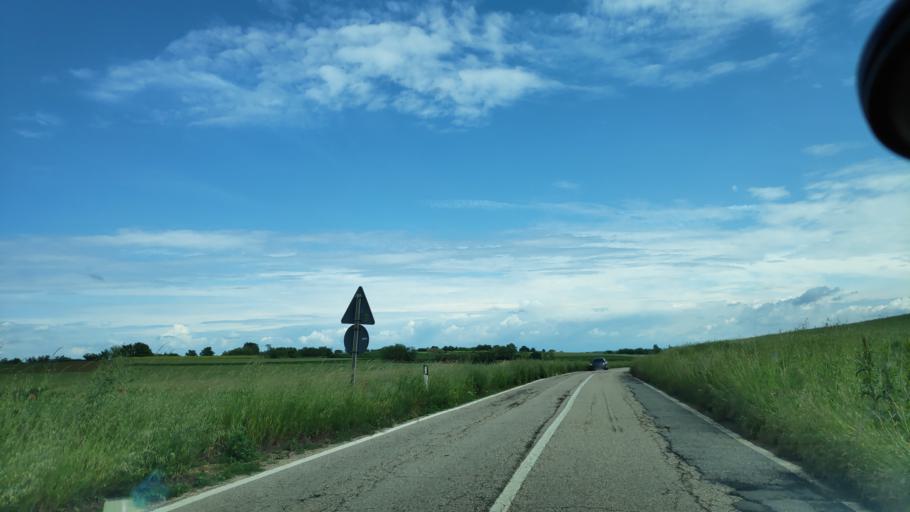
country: IT
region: Piedmont
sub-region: Provincia di Torino
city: Cambiano
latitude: 44.9912
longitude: 7.7765
